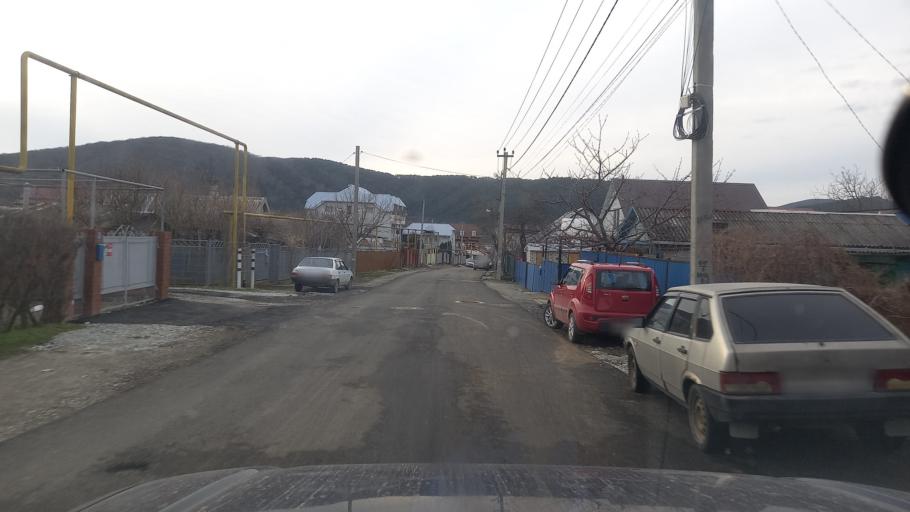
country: RU
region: Krasnodarskiy
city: Arkhipo-Osipovka
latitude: 44.3654
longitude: 38.5343
